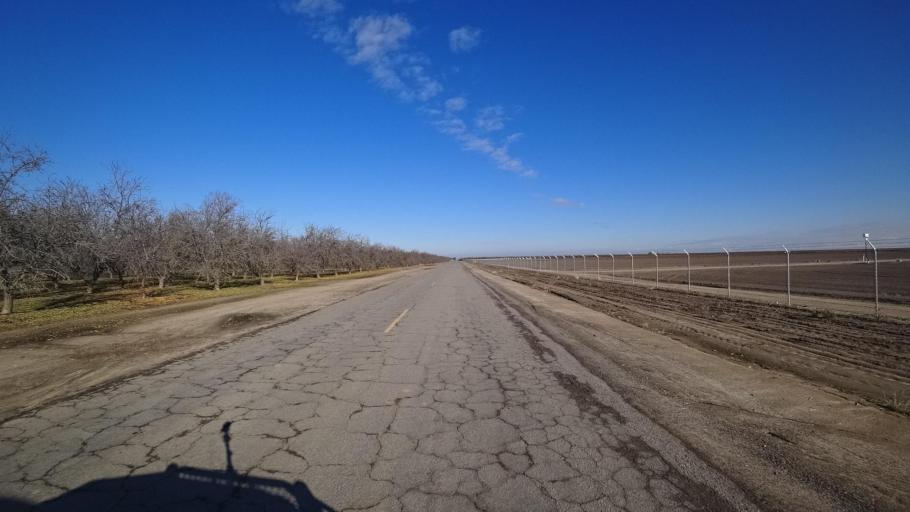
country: US
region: California
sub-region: Kern County
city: McFarland
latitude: 35.6899
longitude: -119.3120
